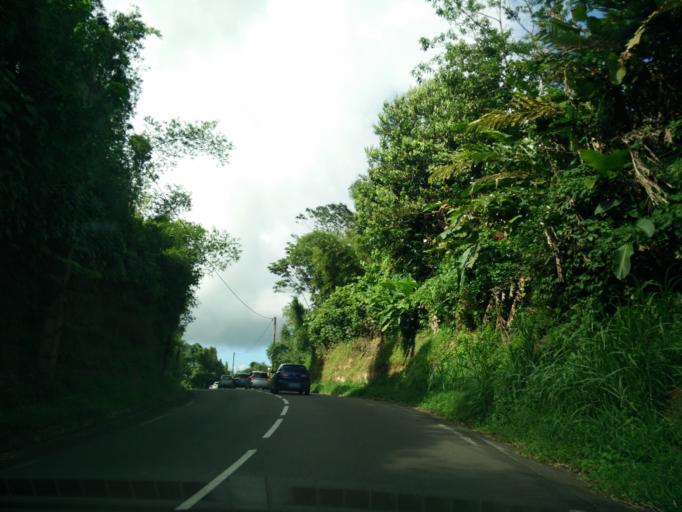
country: MQ
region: Martinique
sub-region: Martinique
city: Le Morne-Rouge
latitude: 14.7954
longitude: -61.1339
